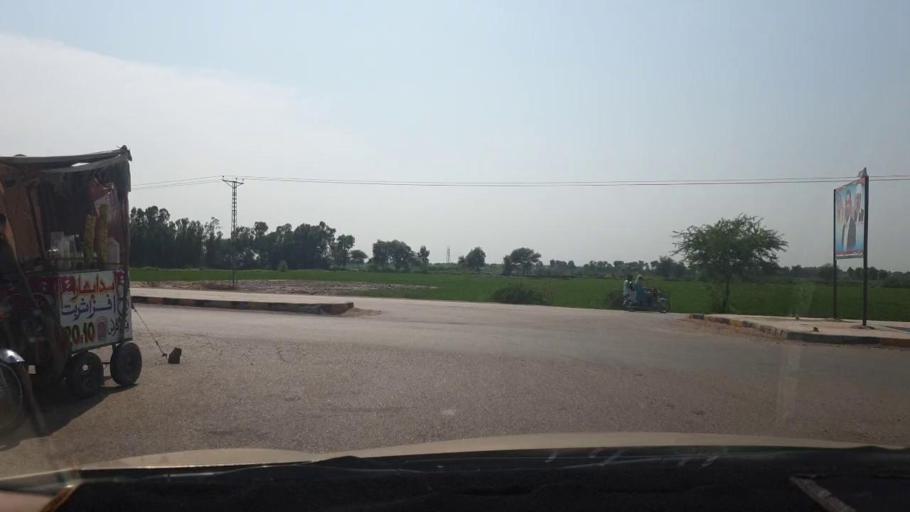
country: PK
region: Sindh
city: Larkana
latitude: 27.6114
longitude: 68.2330
